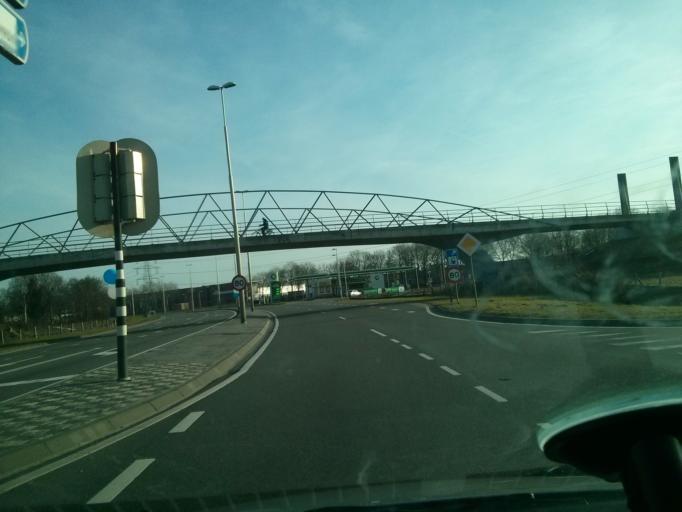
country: NL
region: North Brabant
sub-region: Gemeente Tilburg
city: Tilburg
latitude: 51.5859
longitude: 5.1099
